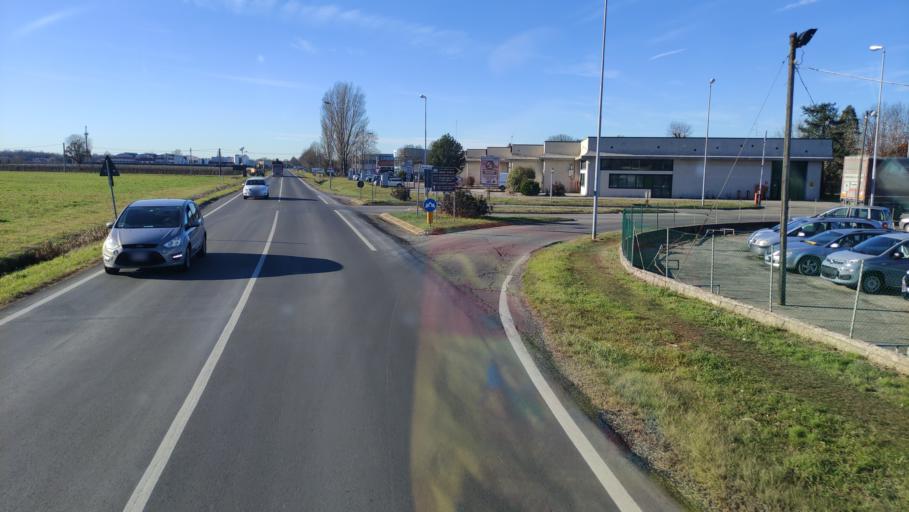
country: IT
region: Emilia-Romagna
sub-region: Provincia di Reggio Emilia
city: Campagnola Emilia
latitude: 44.8351
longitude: 10.7720
